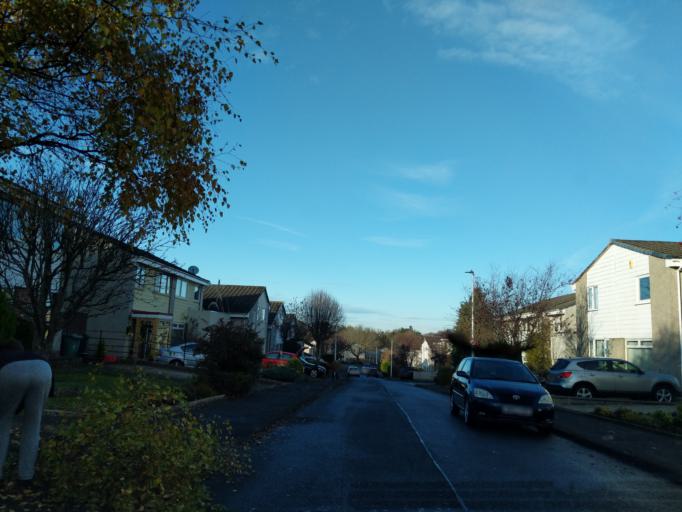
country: GB
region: Scotland
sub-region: Edinburgh
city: Colinton
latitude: 55.9036
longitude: -3.2686
